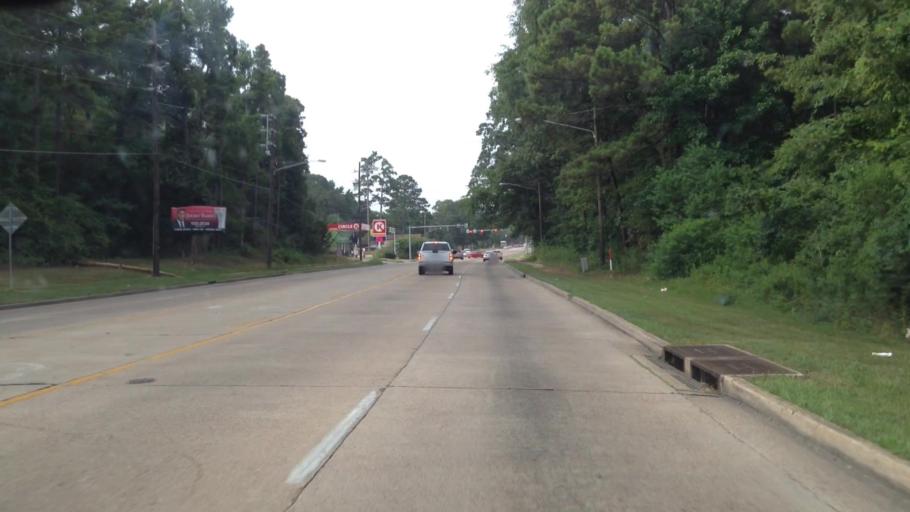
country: US
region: Louisiana
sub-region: Caddo Parish
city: Shreveport
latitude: 32.4143
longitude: -93.8148
